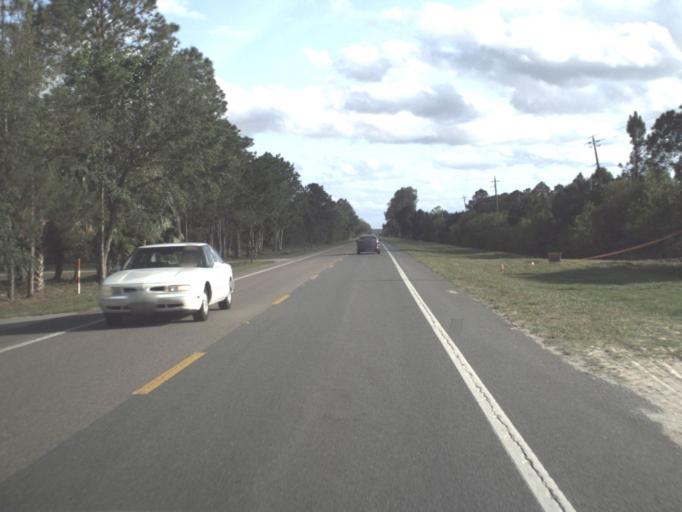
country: US
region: Florida
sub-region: Flagler County
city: Bunnell
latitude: 29.3507
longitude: -81.3112
